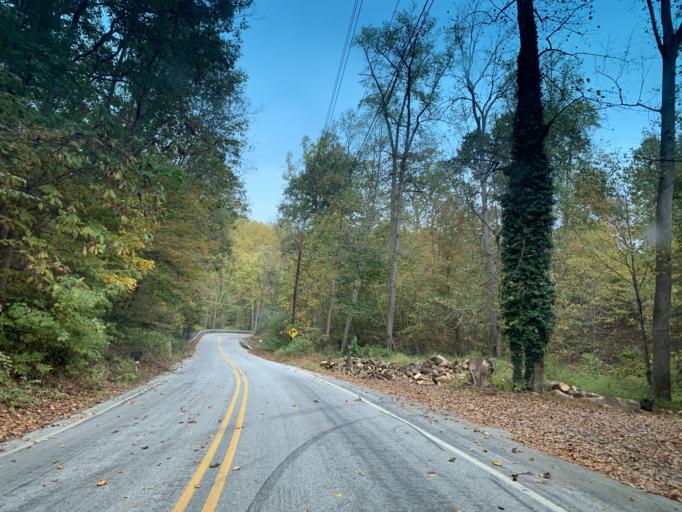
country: US
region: Pennsylvania
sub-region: York County
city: Stewartstown
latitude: 39.8251
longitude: -76.5128
